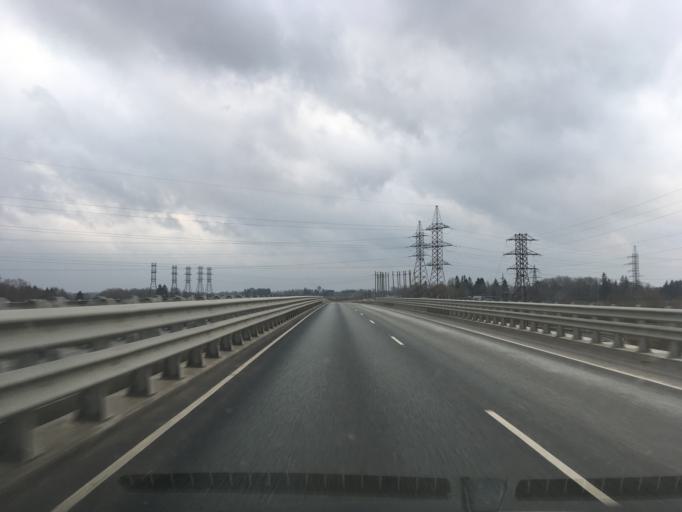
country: EE
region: Harju
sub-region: Joelaehtme vald
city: Loo
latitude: 59.4261
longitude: 24.9205
